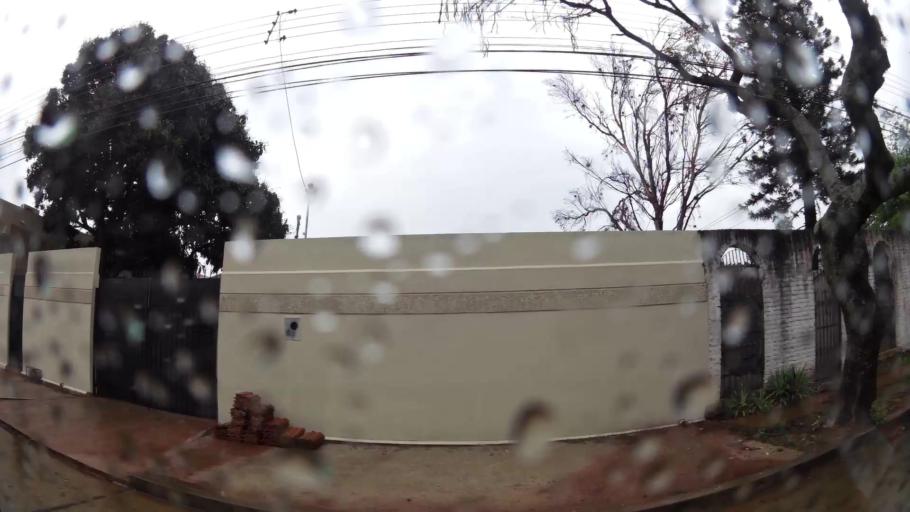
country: BO
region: Santa Cruz
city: Santa Cruz de la Sierra
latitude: -17.7911
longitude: -63.2101
